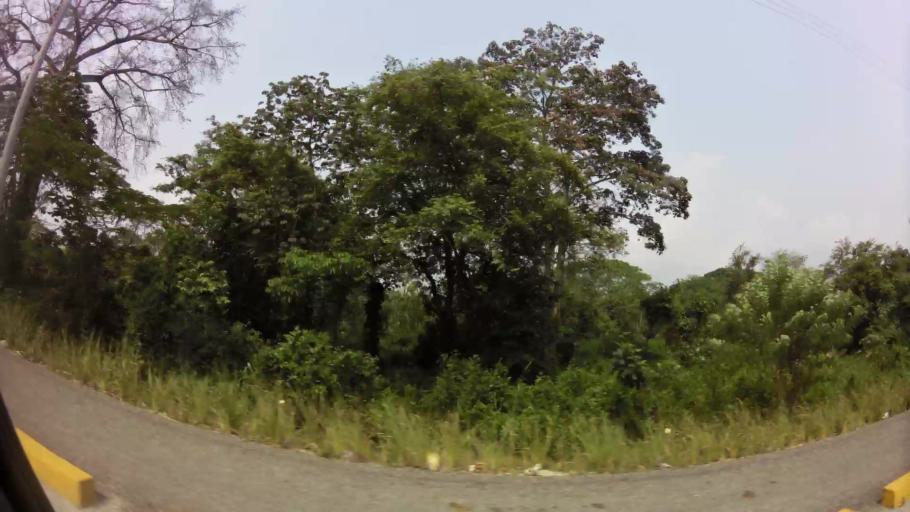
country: HN
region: Cortes
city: San Pedro Sula
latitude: 15.5259
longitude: -88.0042
